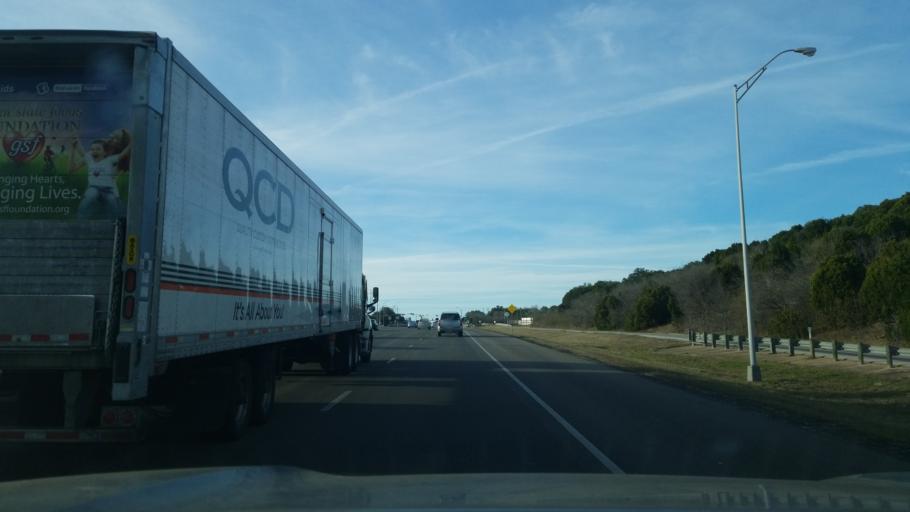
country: US
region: Texas
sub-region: Travis County
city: Rollingwood
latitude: 30.2480
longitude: -97.8054
